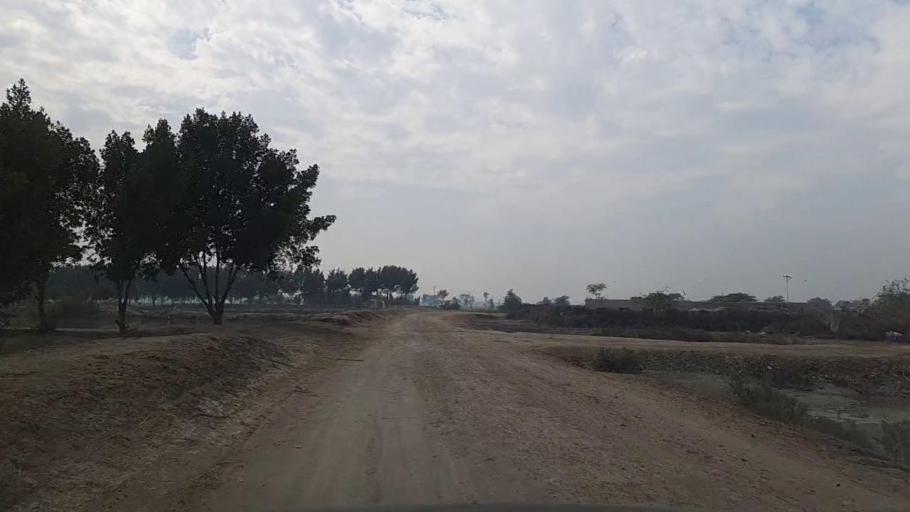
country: PK
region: Sindh
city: Daur
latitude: 26.3717
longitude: 68.3891
